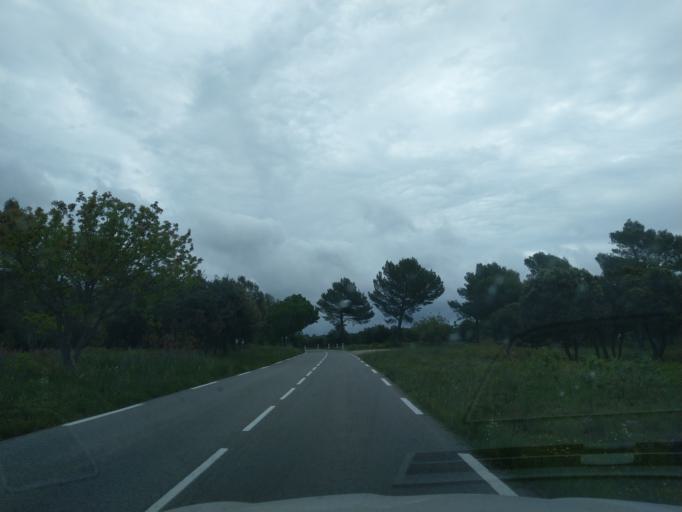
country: FR
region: Provence-Alpes-Cote d'Azur
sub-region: Departement du Var
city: Le Castellet
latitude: 43.2701
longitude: 5.7874
